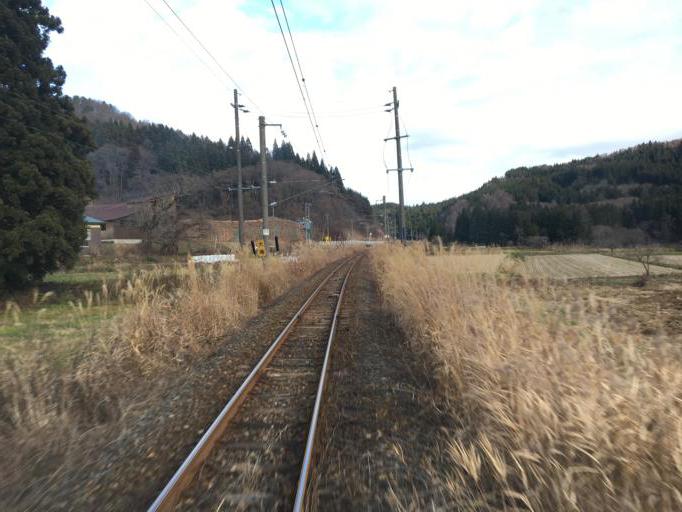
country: JP
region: Yamagata
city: Shinjo
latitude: 38.9685
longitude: 140.3105
